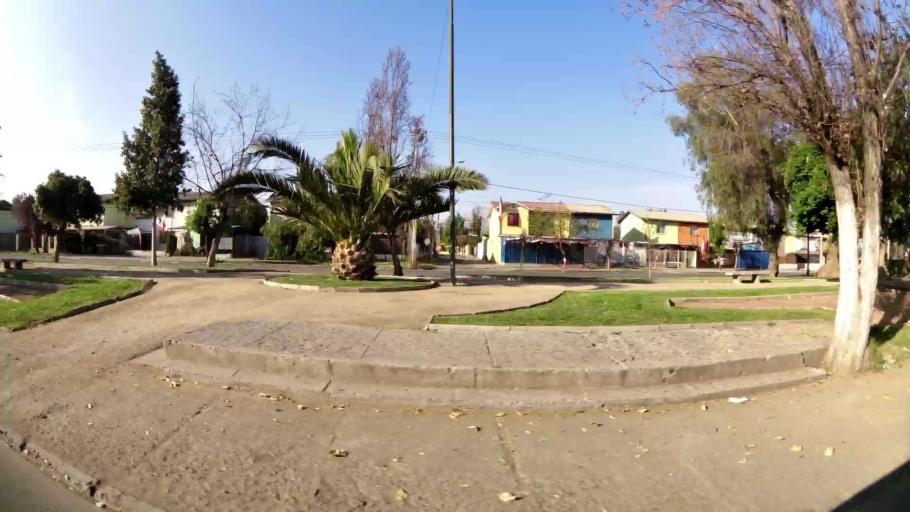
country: CL
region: Santiago Metropolitan
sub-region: Provincia de Santiago
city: Santiago
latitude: -33.3806
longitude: -70.6590
